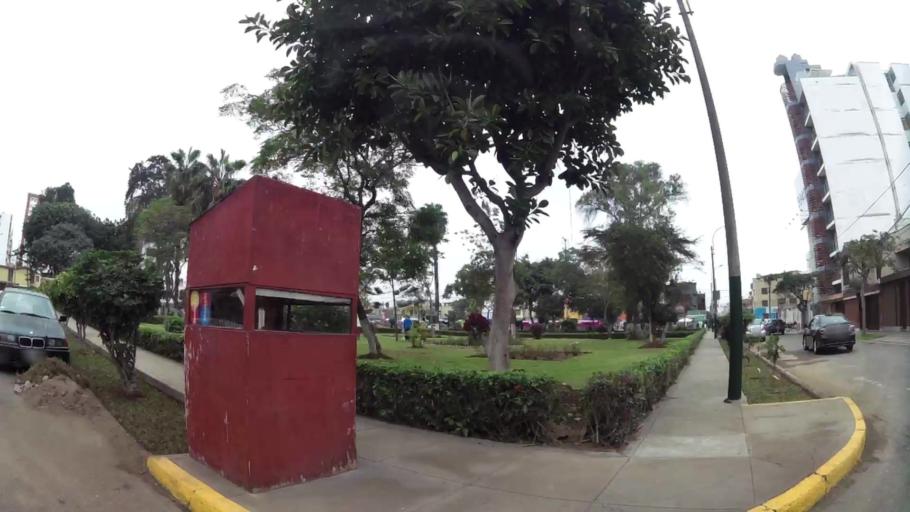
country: PE
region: Lima
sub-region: Lima
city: Surco
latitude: -12.1212
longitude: -77.0056
